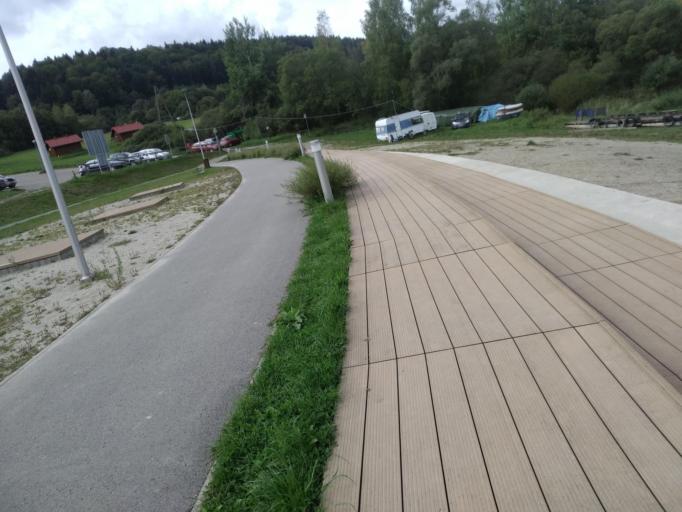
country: PL
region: Lesser Poland Voivodeship
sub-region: Powiat gorlicki
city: Uscie Gorlickie
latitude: 49.5492
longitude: 21.0868
